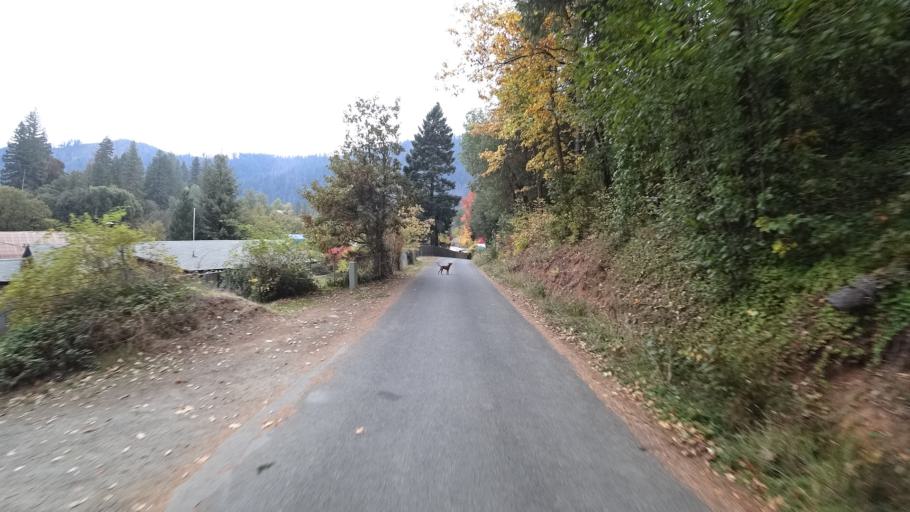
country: US
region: California
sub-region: Siskiyou County
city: Happy Camp
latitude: 41.7984
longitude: -123.3809
